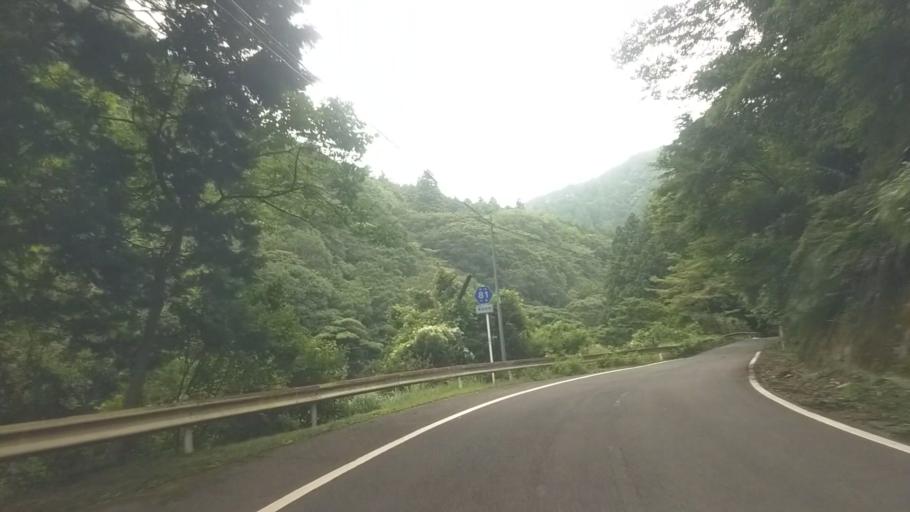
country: JP
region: Chiba
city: Kawaguchi
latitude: 35.2025
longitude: 140.1380
